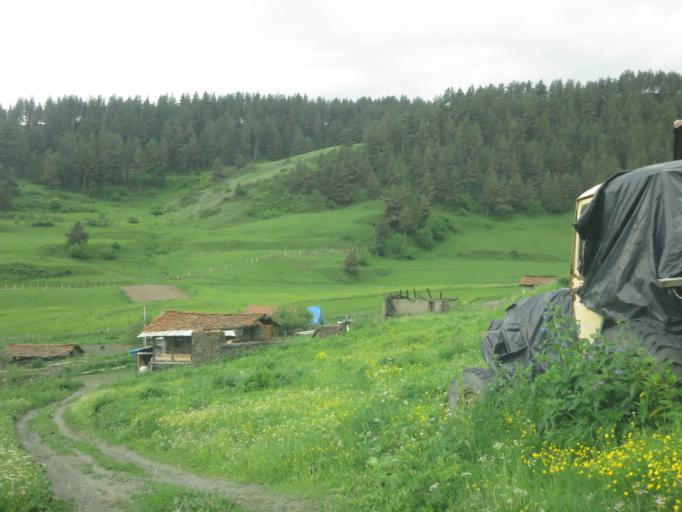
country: RU
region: Chechnya
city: Itum-Kali
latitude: 42.3747
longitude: 45.6587
